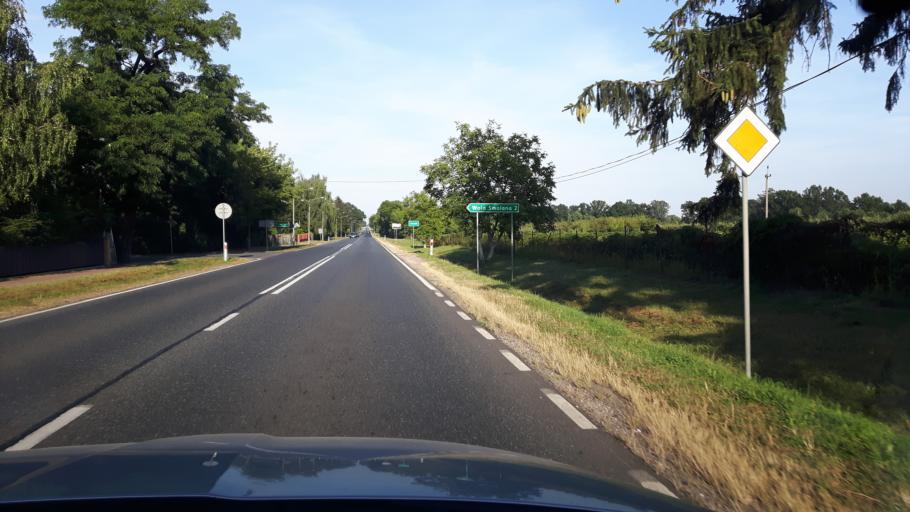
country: PL
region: Masovian Voivodeship
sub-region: Powiat legionowski
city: Wieliszew
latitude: 52.5050
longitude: 20.9919
